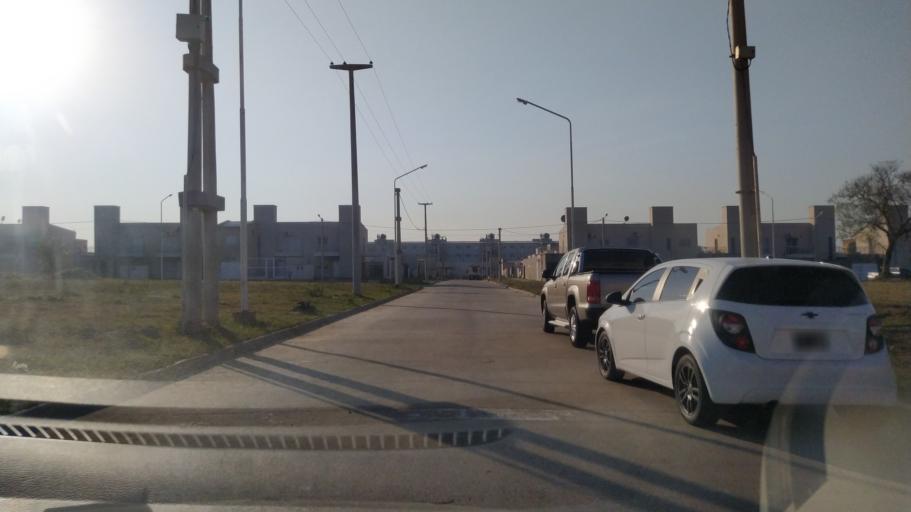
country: AR
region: Corrientes
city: Corrientes
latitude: -27.5231
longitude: -58.8053
